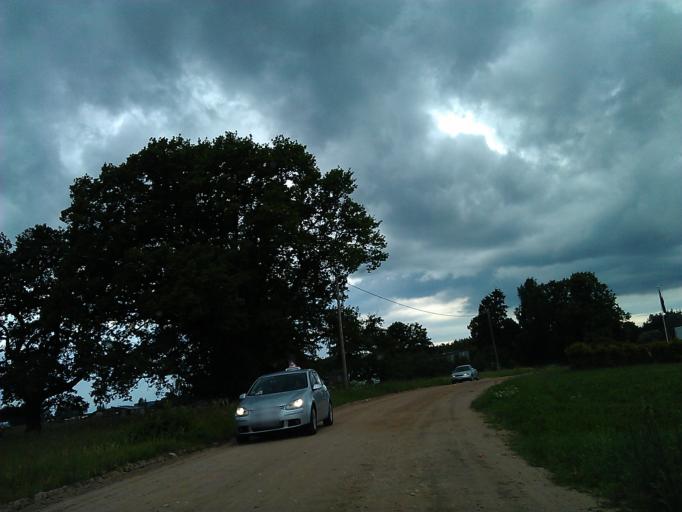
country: LV
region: Adazi
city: Adazi
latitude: 57.0843
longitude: 24.3023
